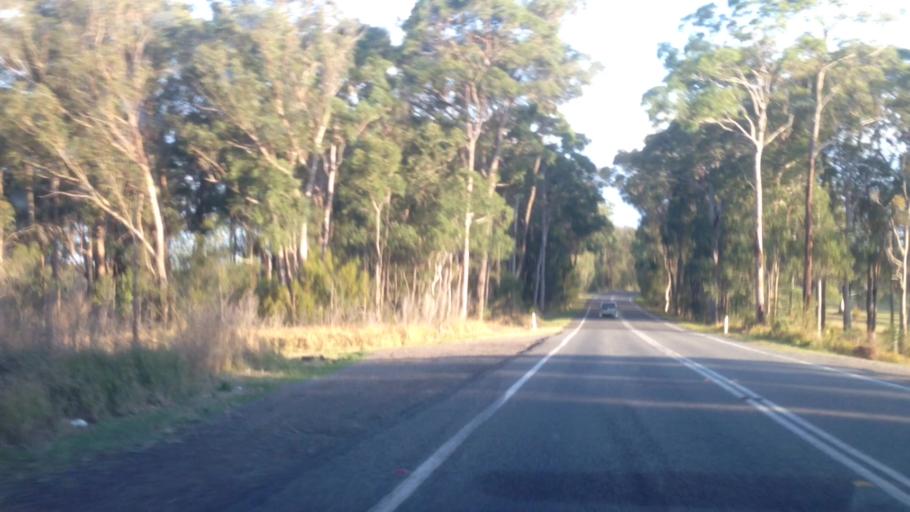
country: AU
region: New South Wales
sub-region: Lake Macquarie Shire
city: Dora Creek
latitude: -33.0201
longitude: 151.4938
